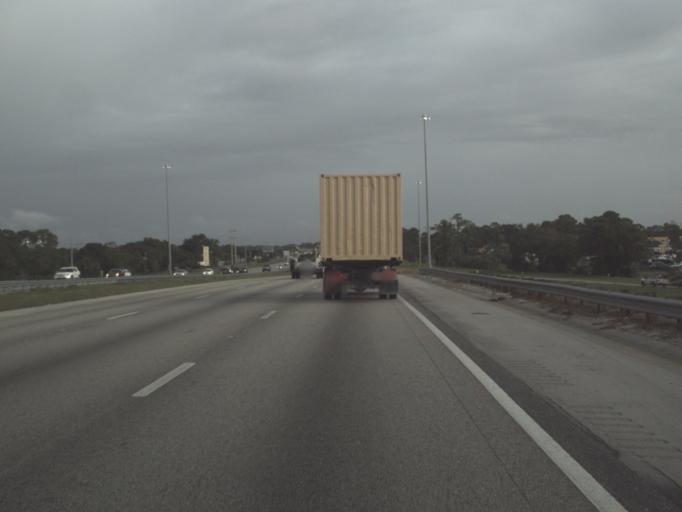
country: US
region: Florida
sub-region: Lee County
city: Tice
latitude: 26.6571
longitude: -81.7993
